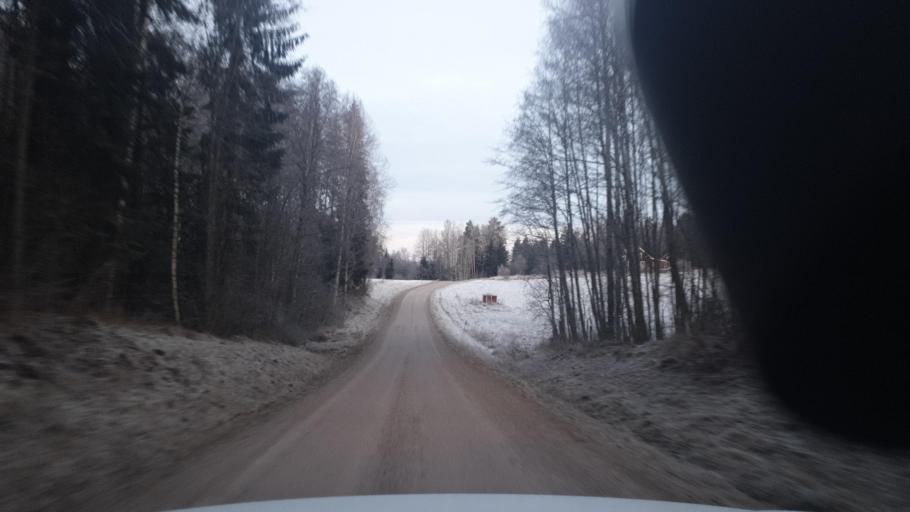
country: SE
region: Vaermland
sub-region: Eda Kommun
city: Amotfors
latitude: 59.8122
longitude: 12.3613
